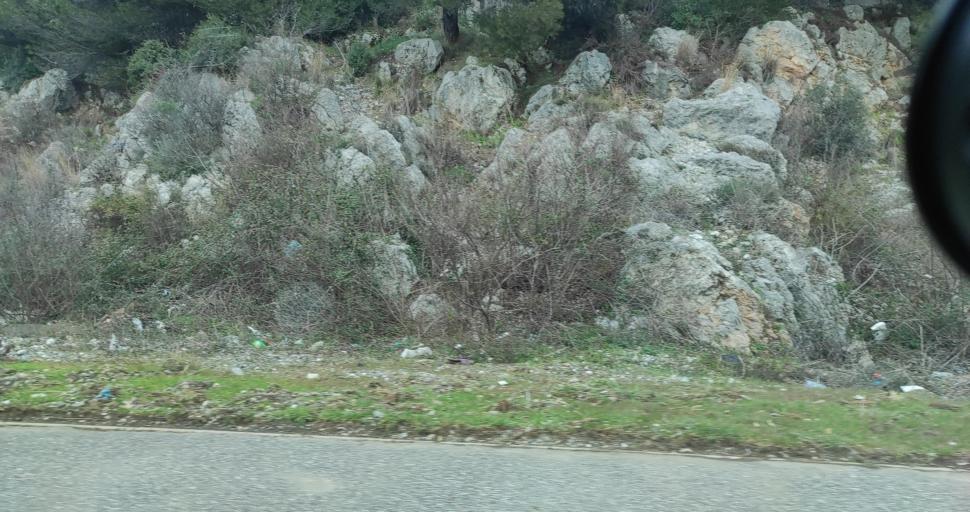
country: AL
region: Lezhe
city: Shengjin
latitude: 41.8080
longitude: 19.6057
